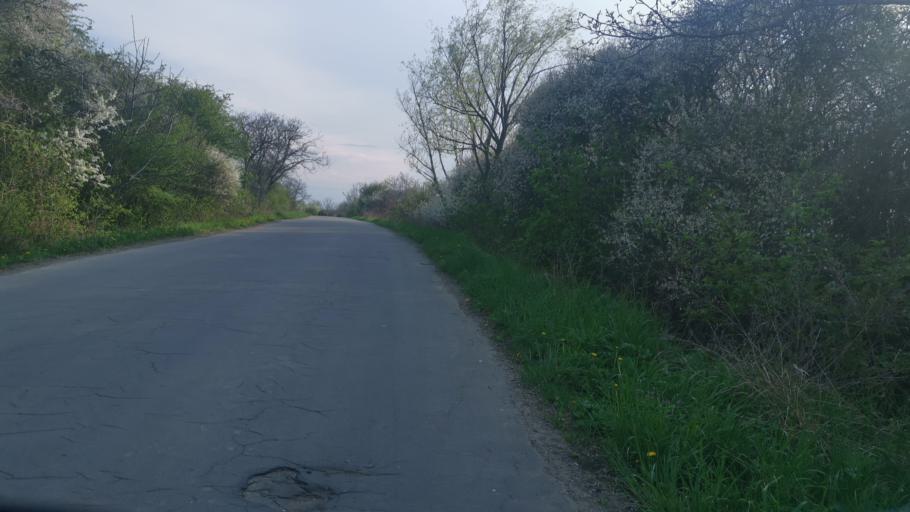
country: CZ
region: South Moravian
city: Petrov
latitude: 48.8536
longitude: 17.3039
